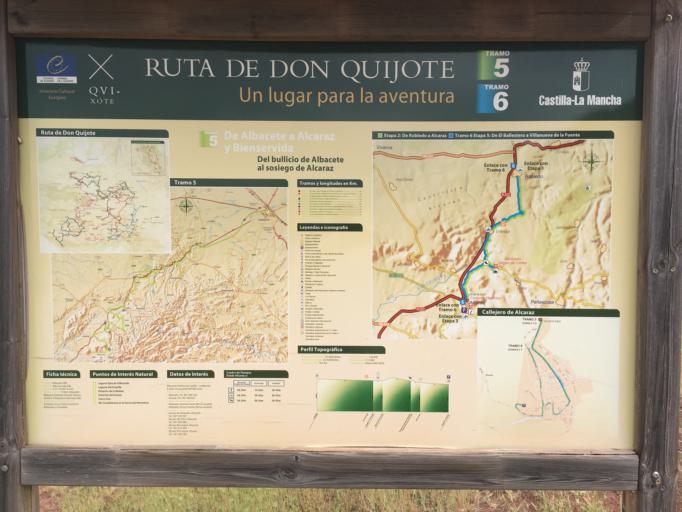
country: ES
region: Castille-La Mancha
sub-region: Provincia de Albacete
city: Alcaraz
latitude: 38.6808
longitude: -2.4952
